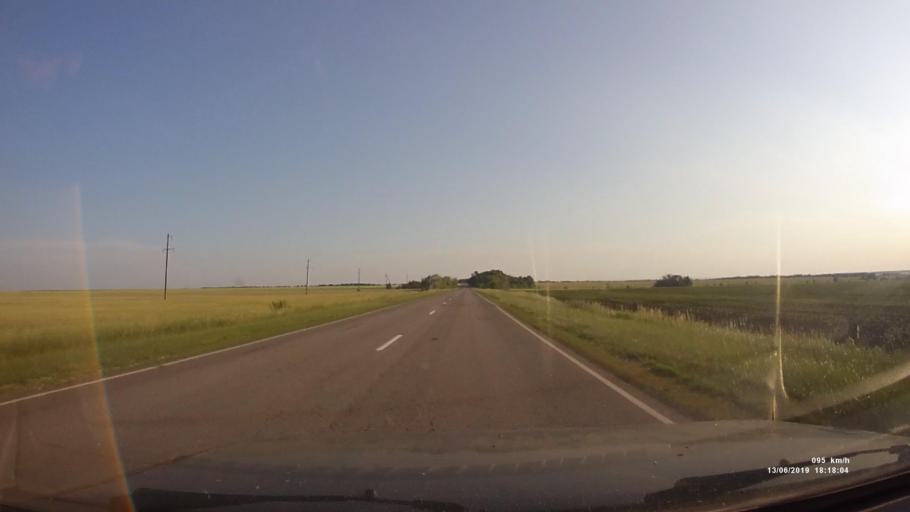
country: RU
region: Rostov
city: Kazanskaya
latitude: 49.9124
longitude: 41.3180
